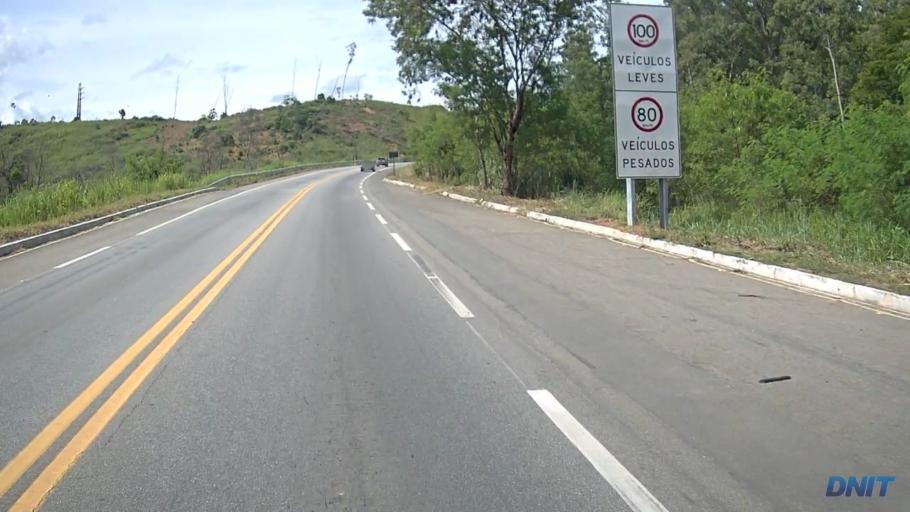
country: BR
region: Minas Gerais
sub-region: Ipatinga
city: Ipatinga
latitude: -19.4372
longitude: -42.5103
